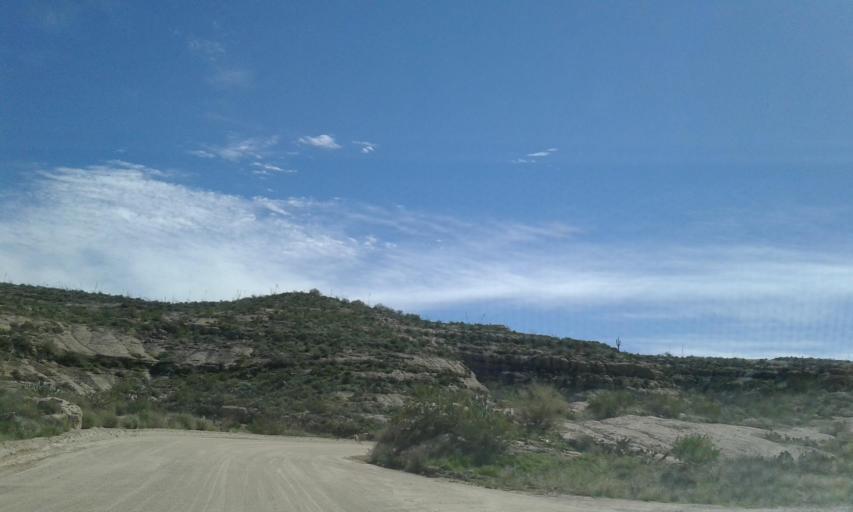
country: US
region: Arizona
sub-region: Pinal County
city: Gold Camp
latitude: 33.5263
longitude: -111.3193
